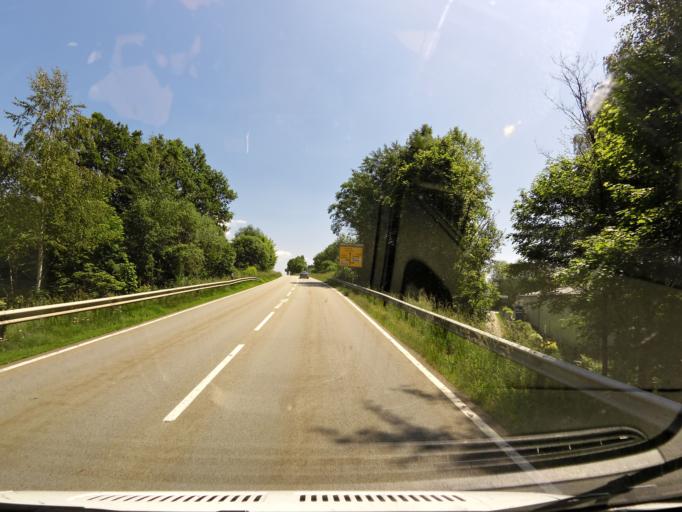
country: DE
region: Bavaria
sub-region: Lower Bavaria
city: Hutthurm
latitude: 48.6786
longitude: 13.4797
